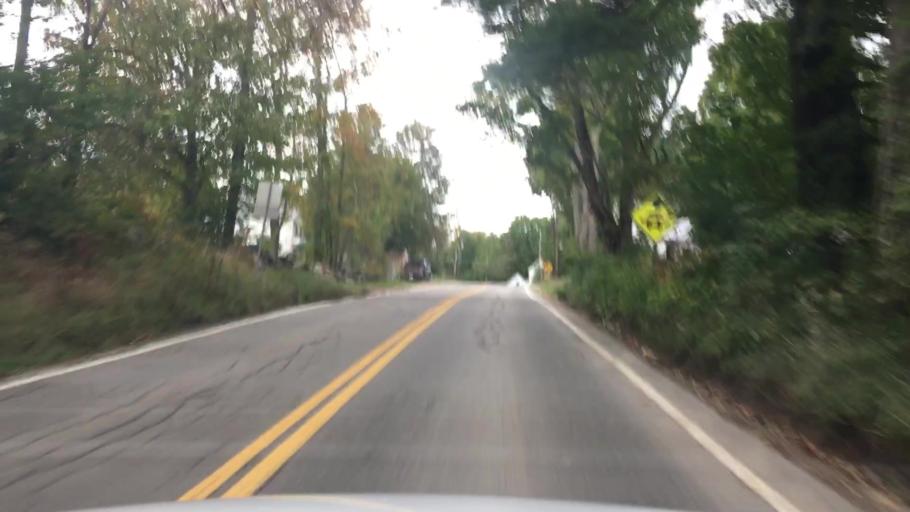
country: US
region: New Hampshire
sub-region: Carroll County
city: Effingham
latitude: 43.7600
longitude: -70.9978
